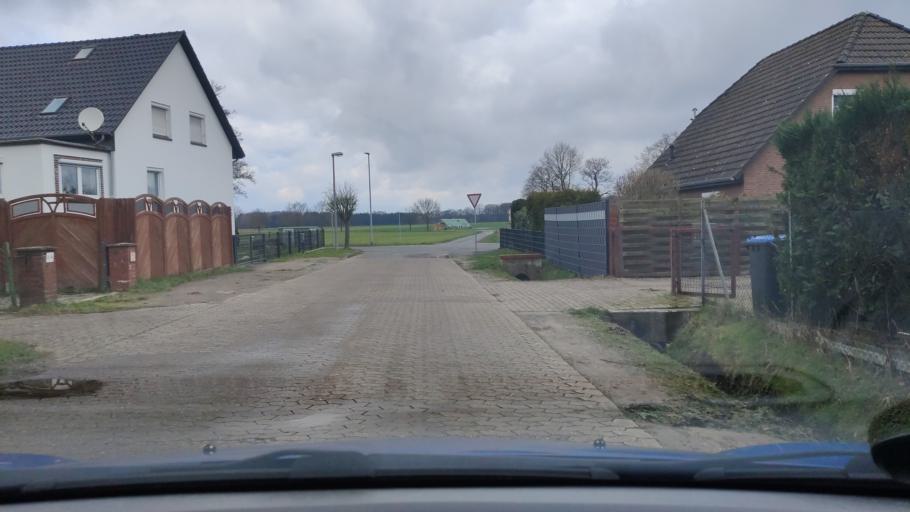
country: DE
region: Lower Saxony
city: Langenhagen
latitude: 52.4753
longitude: 9.7177
